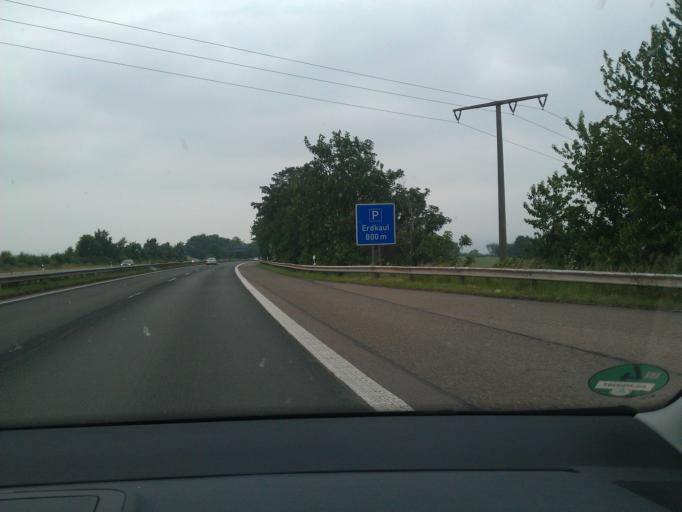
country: DE
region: Rheinland-Pfalz
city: Mulheim-Karlich
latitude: 50.3672
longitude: 7.4970
